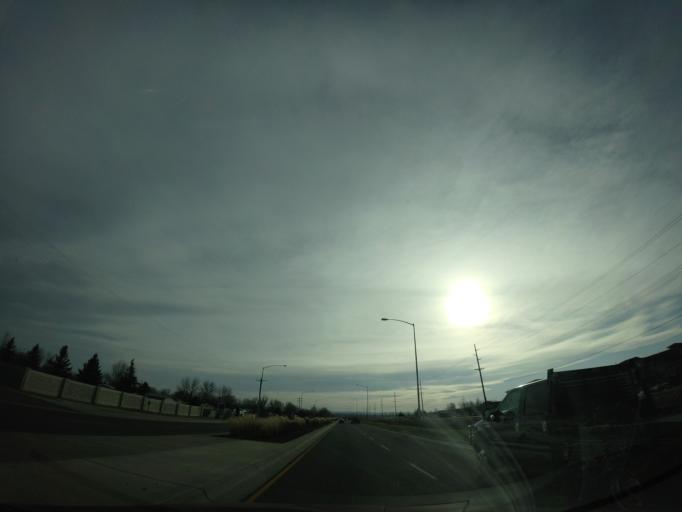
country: US
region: Montana
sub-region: Yellowstone County
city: Billings
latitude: 45.7670
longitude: -108.6177
